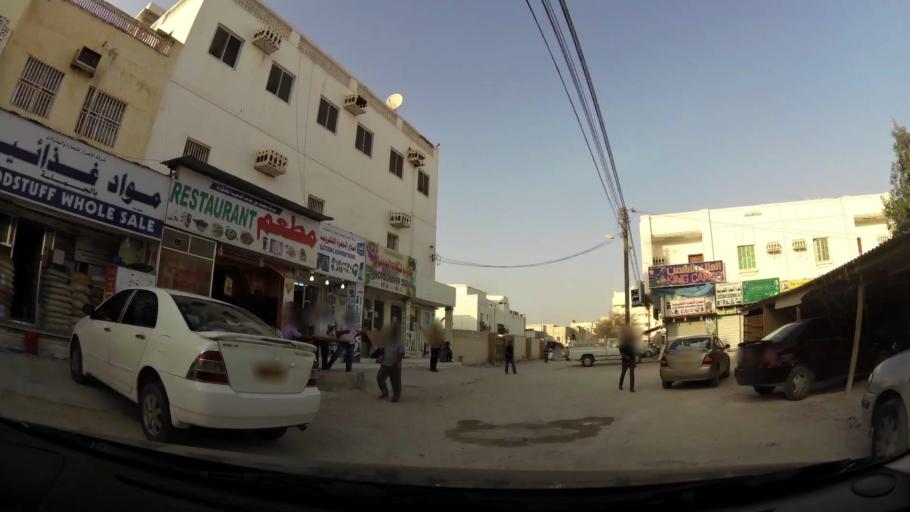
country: OM
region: Zufar
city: Salalah
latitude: 17.0129
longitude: 54.0971
